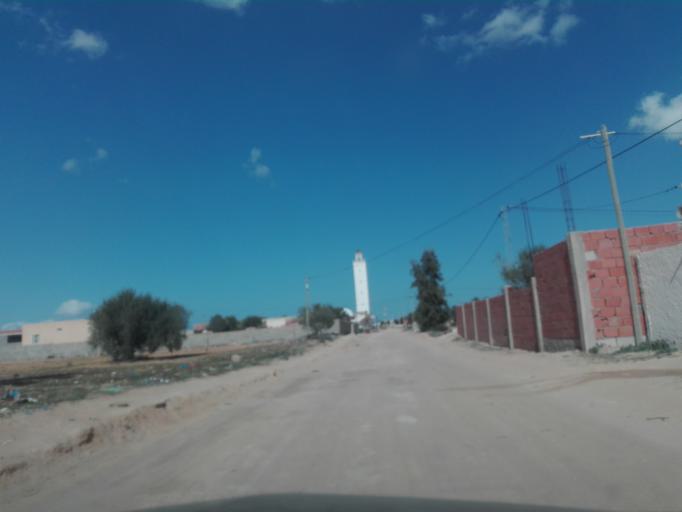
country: TN
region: Madanin
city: Bin Qirdan
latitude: 33.1588
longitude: 11.1945
